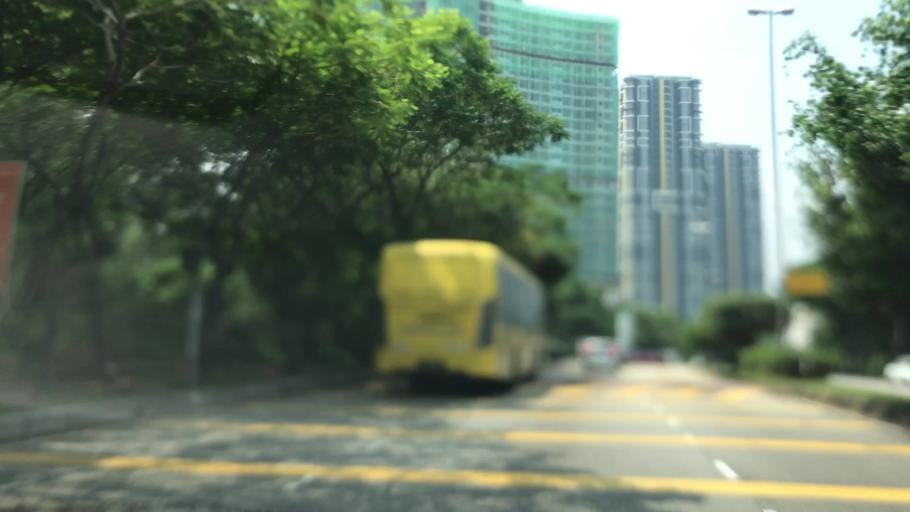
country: MY
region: Selangor
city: Subang Jaya
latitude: 3.0241
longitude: 101.6211
